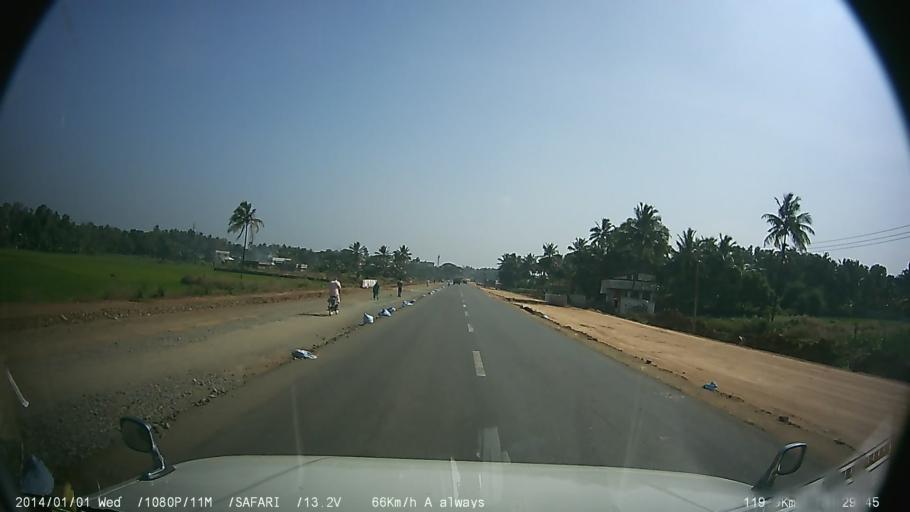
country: IN
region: Kerala
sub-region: Palakkad district
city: Palakkad
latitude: 10.6434
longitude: 76.5366
